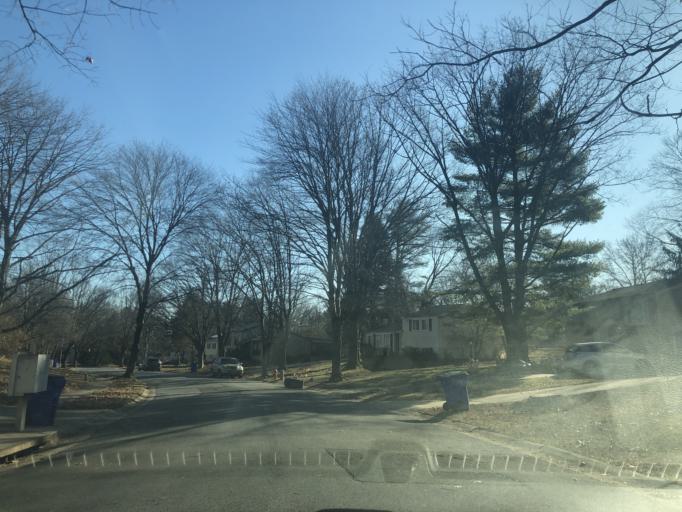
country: US
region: Maryland
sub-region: Howard County
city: Columbia
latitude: 39.2015
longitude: -76.8276
